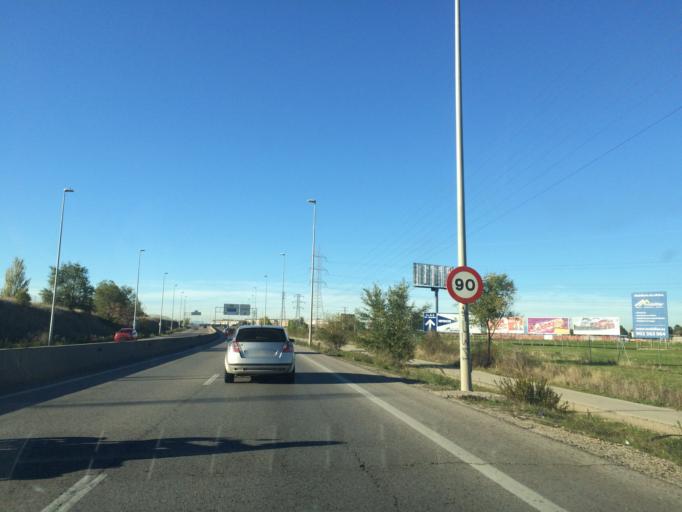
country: ES
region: Madrid
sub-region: Provincia de Madrid
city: Mostoles
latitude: 40.3280
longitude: -3.8492
